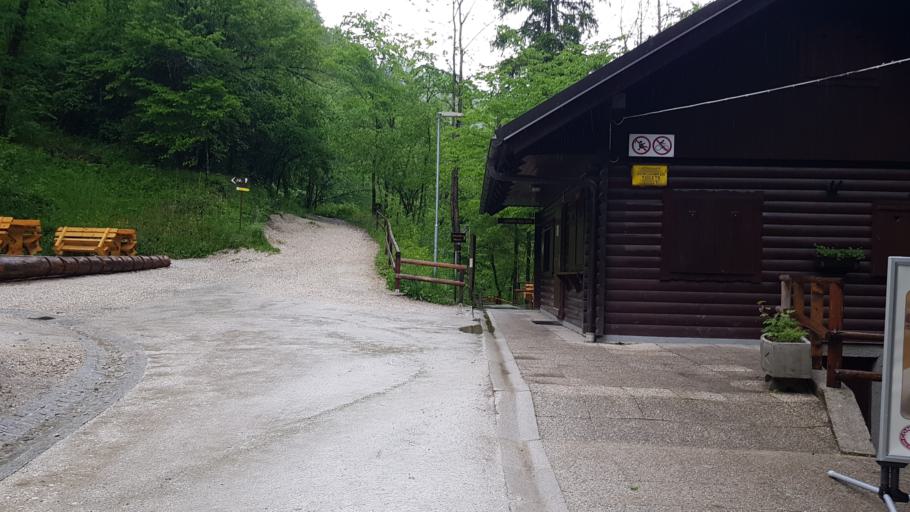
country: SI
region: Gorje
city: Zgornje Gorje
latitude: 46.3935
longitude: 14.0856
